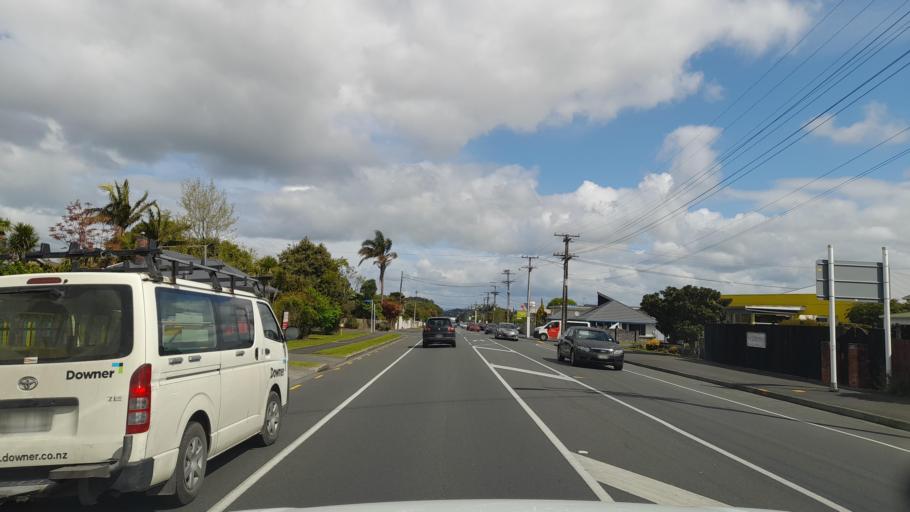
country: NZ
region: Northland
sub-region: Whangarei
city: Whangarei
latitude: -35.7099
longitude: 174.3219
